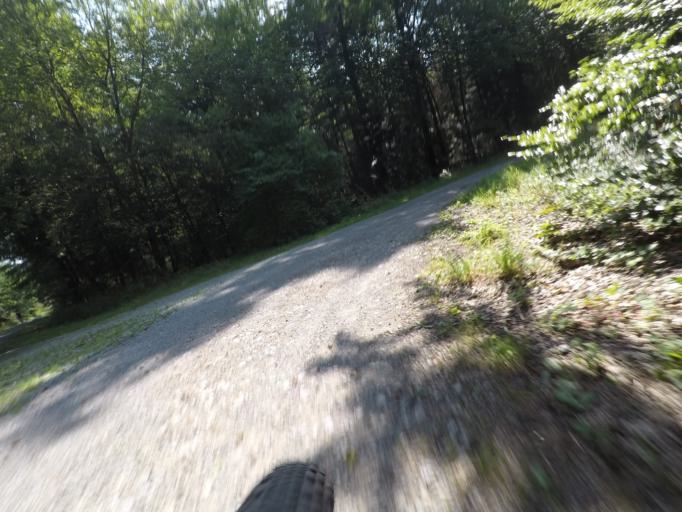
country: DE
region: Baden-Wuerttemberg
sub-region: Regierungsbezirk Stuttgart
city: Steinenbronn
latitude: 48.6835
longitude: 9.1102
